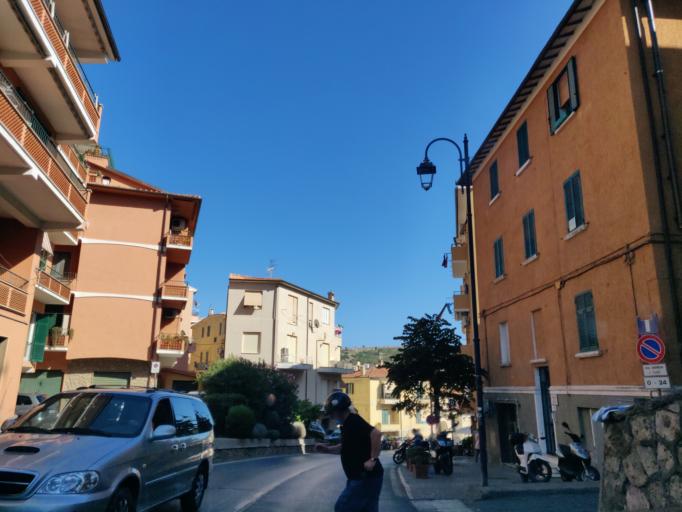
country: IT
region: Tuscany
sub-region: Provincia di Grosseto
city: Porto Ercole
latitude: 42.3956
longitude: 11.2030
